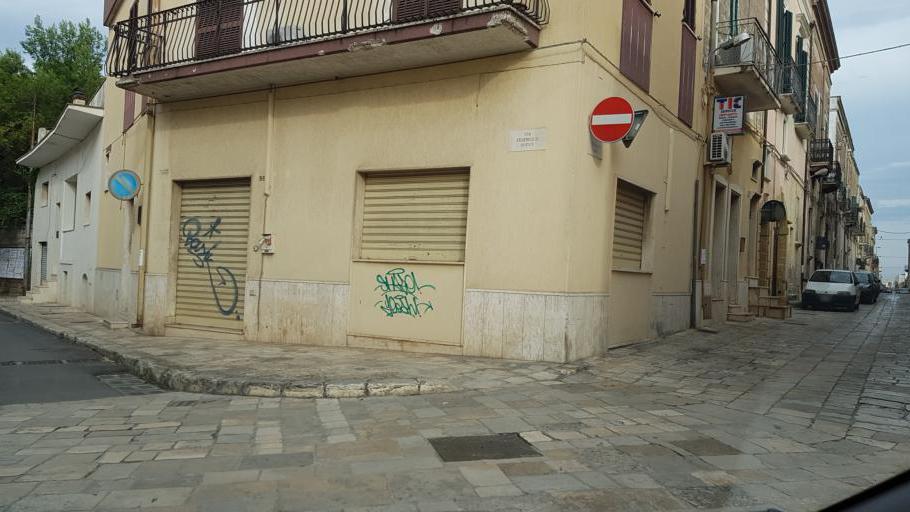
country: IT
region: Apulia
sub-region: Provincia di Brindisi
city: Mesagne
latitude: 40.5582
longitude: 17.8109
